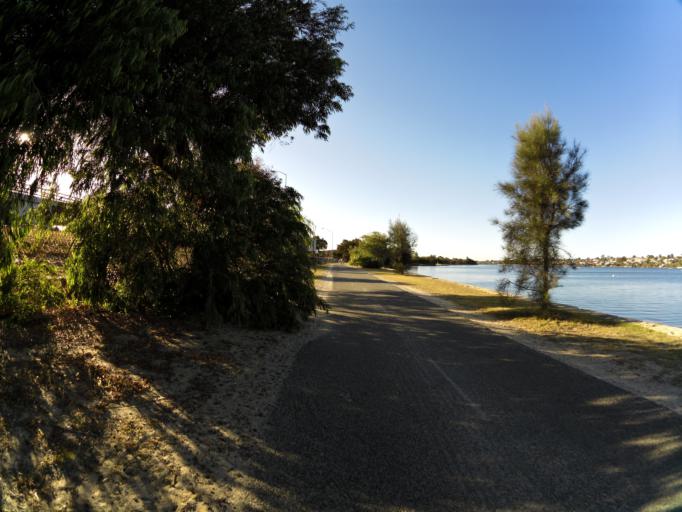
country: AU
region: Western Australia
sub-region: South Perth
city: Manning
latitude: -32.0130
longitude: 115.8567
